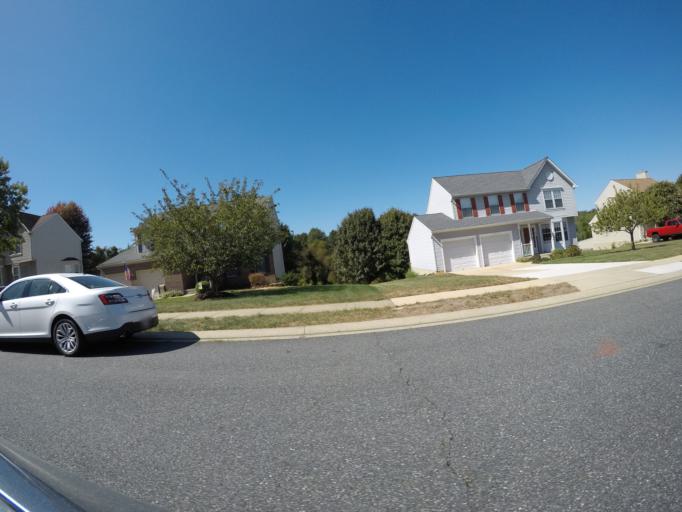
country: US
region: Maryland
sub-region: Harford County
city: Riverside
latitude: 39.4738
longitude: -76.2764
